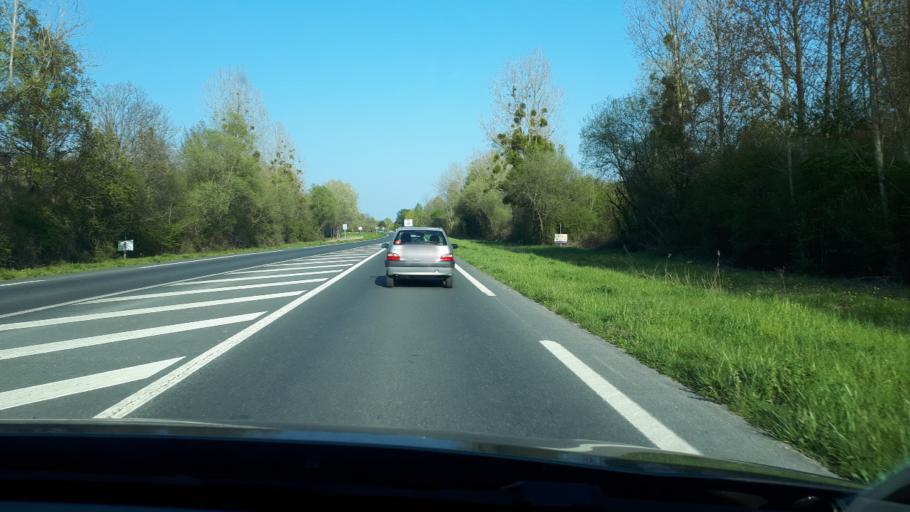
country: FR
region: Centre
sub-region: Departement du Loir-et-Cher
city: Saint-Georges-sur-Cher
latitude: 47.3274
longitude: 1.1256
